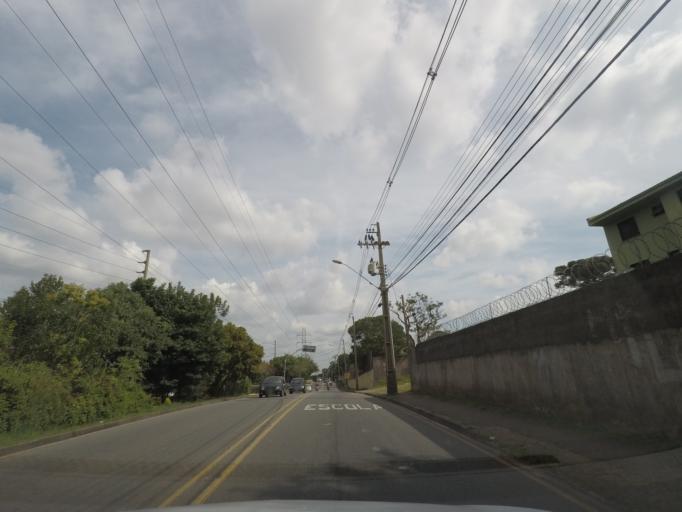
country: BR
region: Parana
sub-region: Pinhais
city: Pinhais
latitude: -25.4818
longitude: -49.2125
